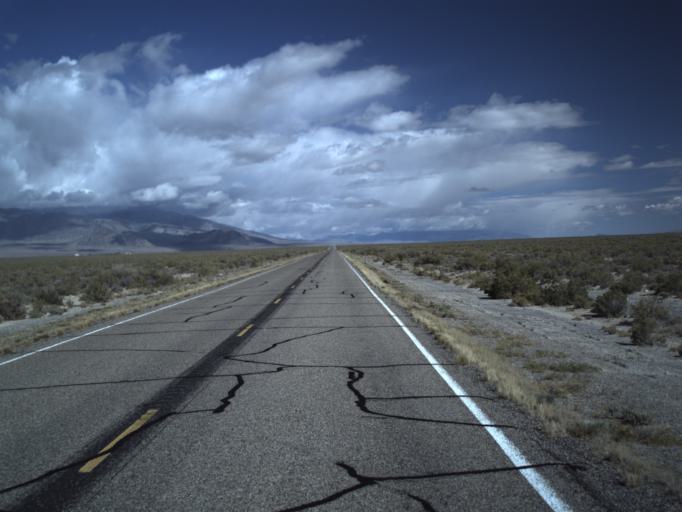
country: US
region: Nevada
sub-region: White Pine County
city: McGill
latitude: 39.0150
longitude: -114.0352
